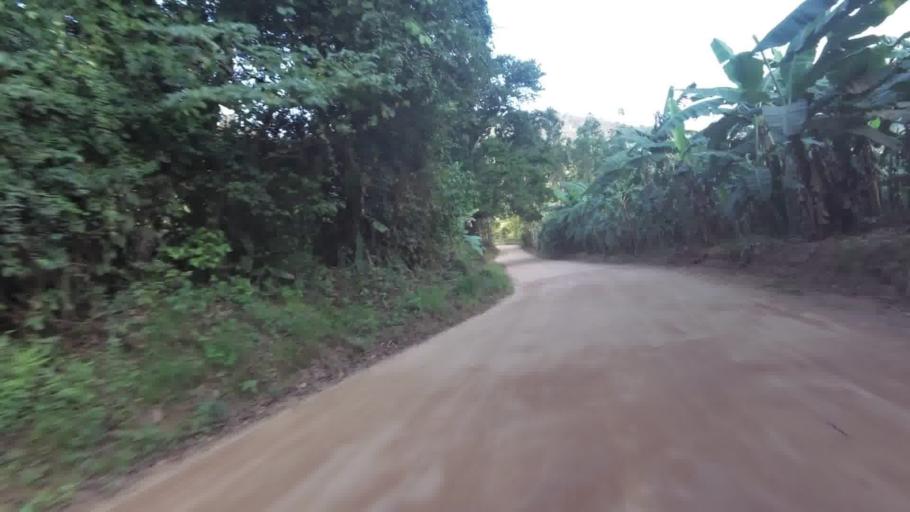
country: BR
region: Espirito Santo
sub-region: Alfredo Chaves
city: Alfredo Chaves
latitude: -20.5912
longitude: -40.6985
